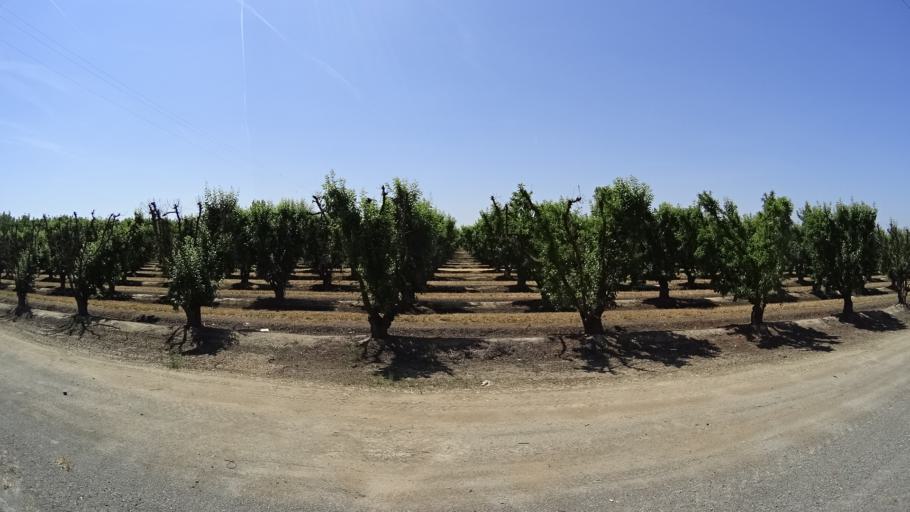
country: US
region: California
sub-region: Kings County
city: Lucerne
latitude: 36.4012
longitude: -119.6165
